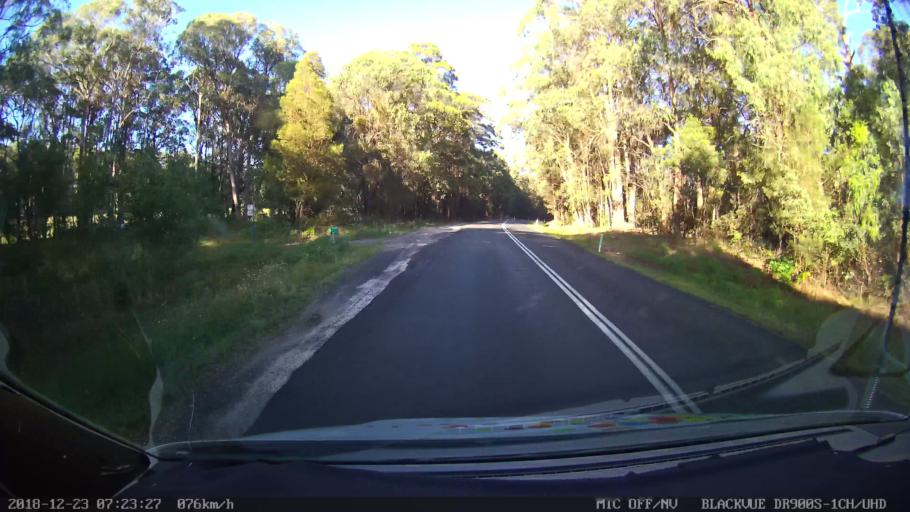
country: AU
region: New South Wales
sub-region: Armidale Dumaresq
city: Enmore
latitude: -30.5062
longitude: 152.2357
